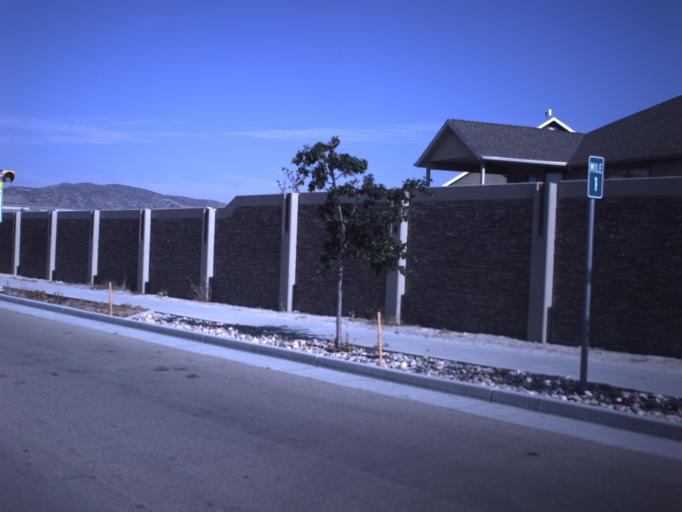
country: US
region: Utah
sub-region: Utah County
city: Lehi
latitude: 40.4133
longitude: -111.8854
